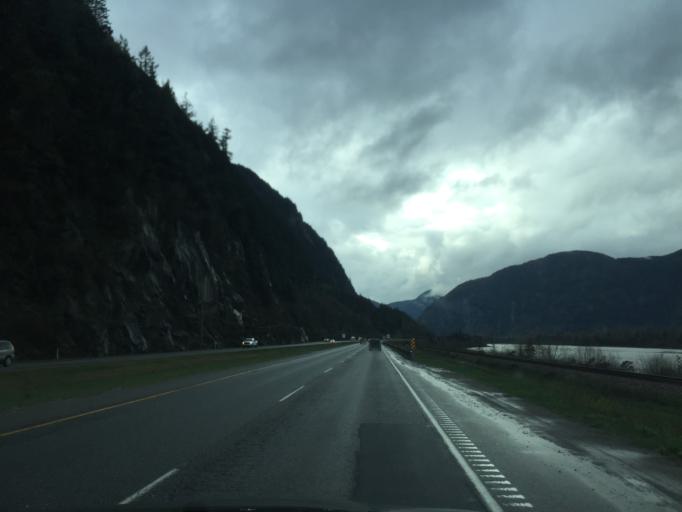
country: CA
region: British Columbia
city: Hope
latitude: 49.3647
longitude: -121.5283
